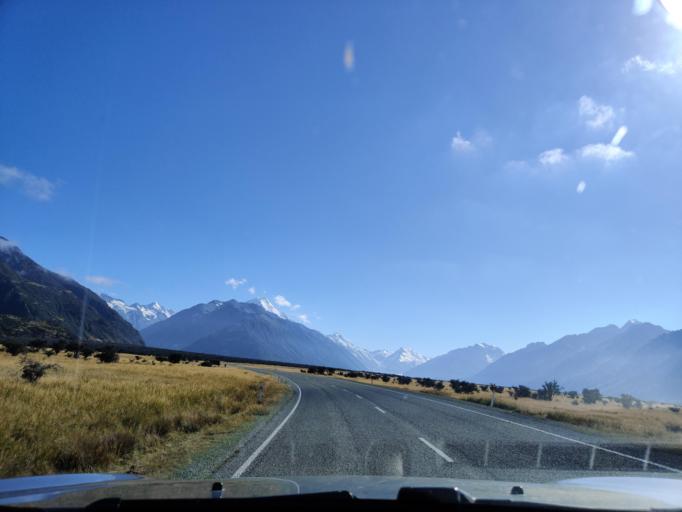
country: NZ
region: Canterbury
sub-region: Timaru District
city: Pleasant Point
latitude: -43.7905
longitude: 170.1194
